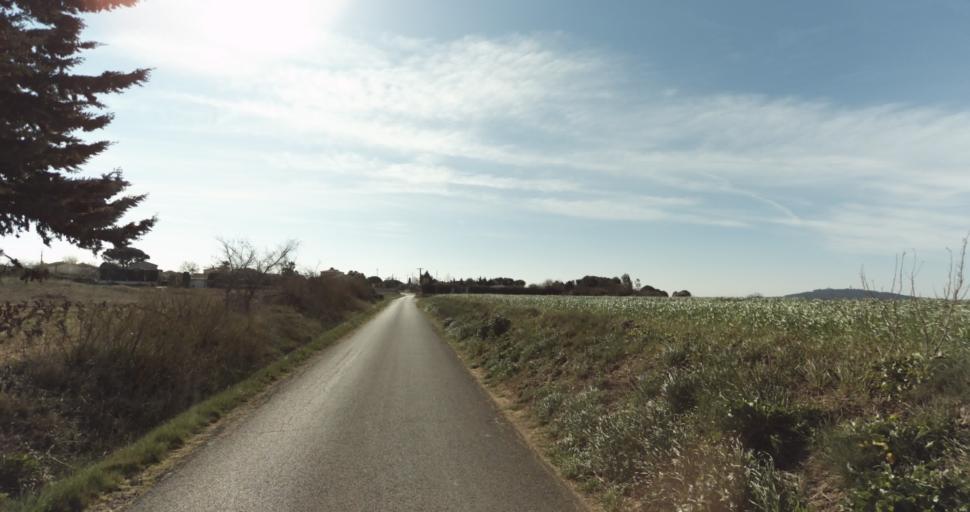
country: FR
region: Languedoc-Roussillon
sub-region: Departement de l'Herault
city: Marseillan
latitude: 43.3378
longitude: 3.5139
